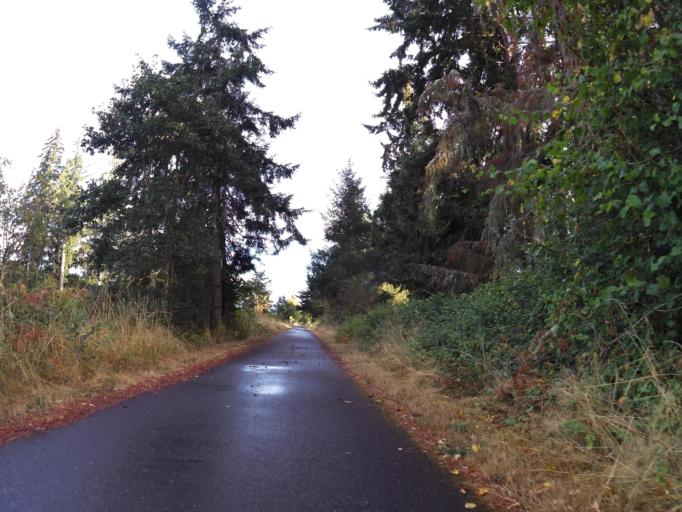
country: US
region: Washington
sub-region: Thurston County
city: Rainier
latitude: 46.8980
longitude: -122.7562
